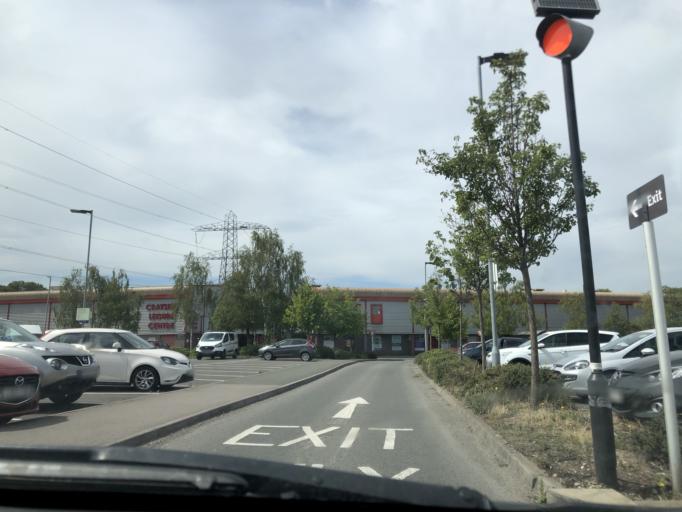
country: GB
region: England
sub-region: Greater London
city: Bexley
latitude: 51.4491
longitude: 0.1775
